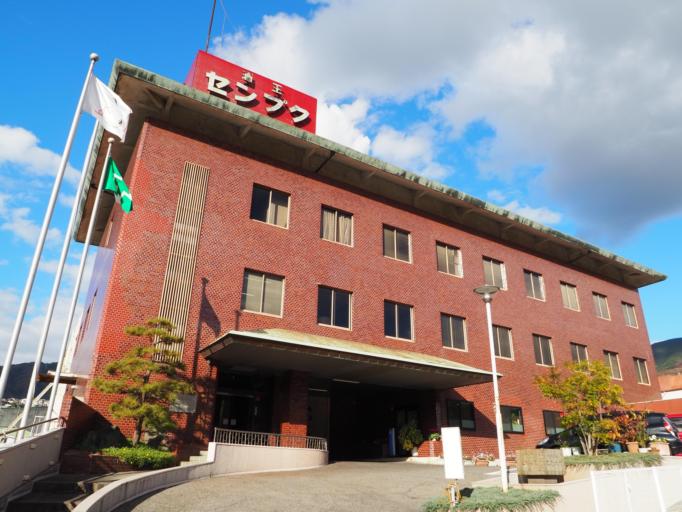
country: JP
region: Hiroshima
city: Kure
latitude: 34.2510
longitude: 132.5776
